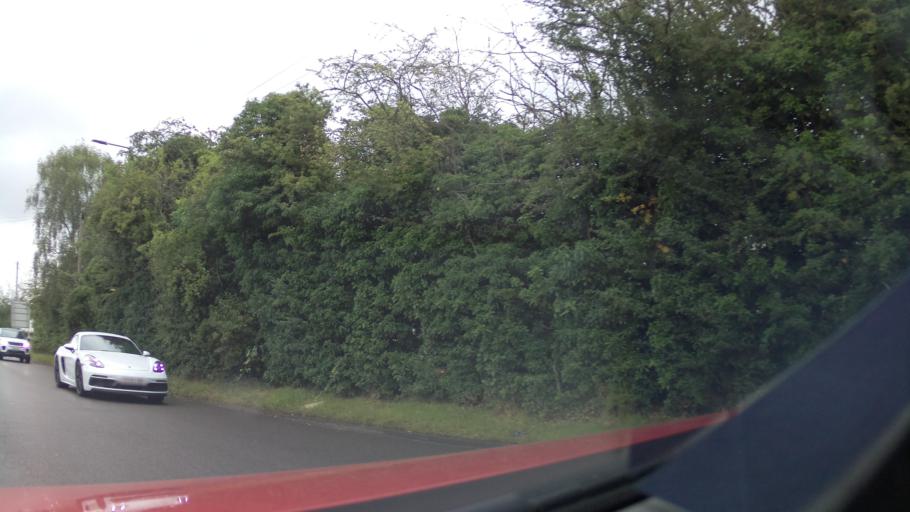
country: GB
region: England
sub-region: Solihull
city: Shirley
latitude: 52.3943
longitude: -1.8236
